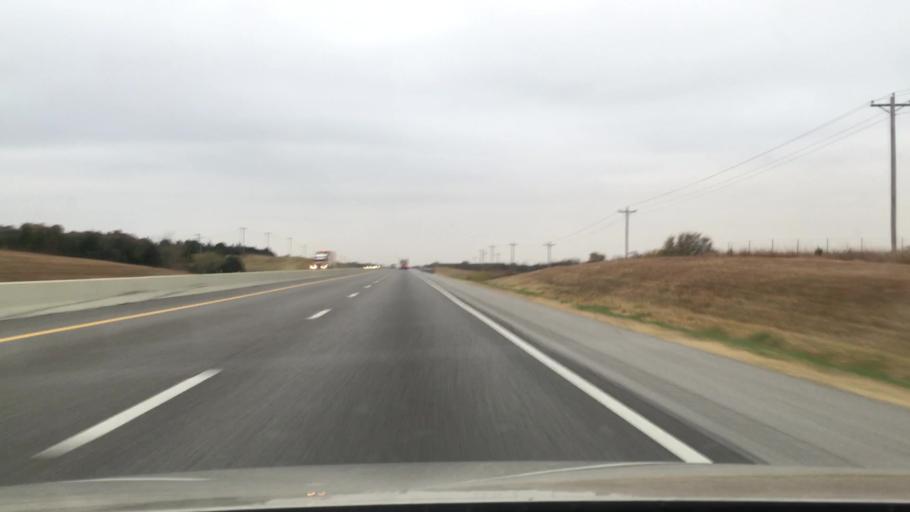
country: US
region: Oklahoma
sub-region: Lincoln County
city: Chandler
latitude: 35.7356
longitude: -96.7936
